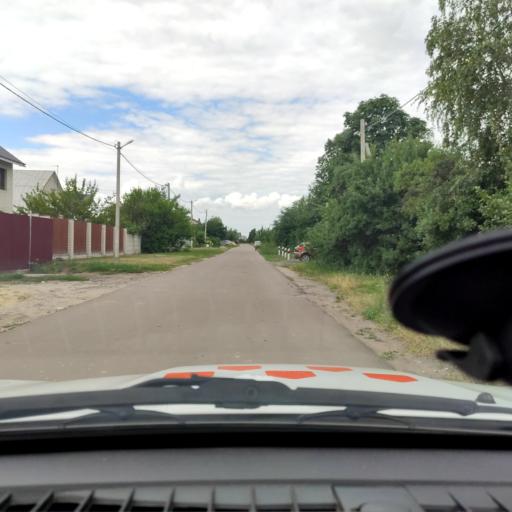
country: RU
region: Voronezj
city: Ramon'
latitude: 51.8287
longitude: 39.2592
